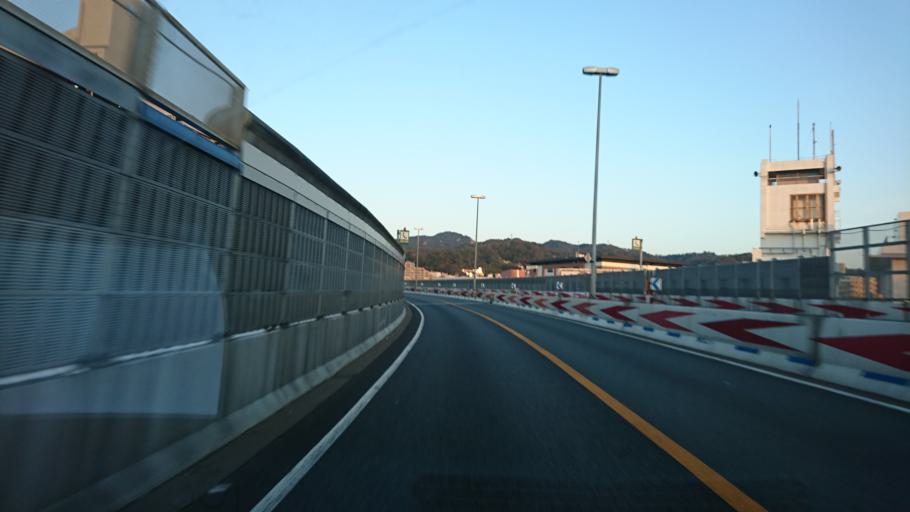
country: JP
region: Hyogo
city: Kobe
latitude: 34.6495
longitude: 135.1303
